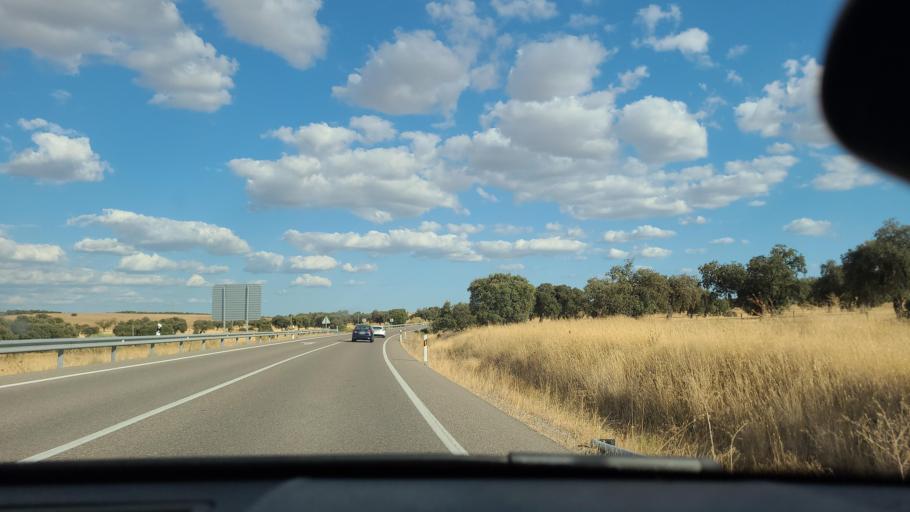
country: ES
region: Extremadura
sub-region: Provincia de Badajoz
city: Granja de Torrehermosa
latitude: 38.2877
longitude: -5.5244
